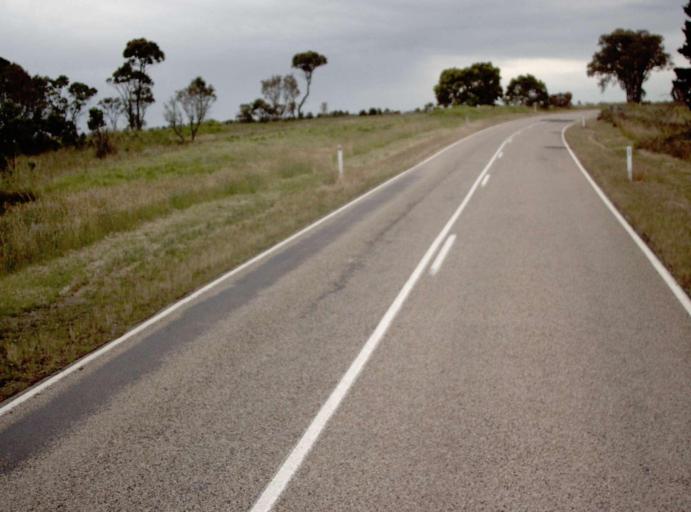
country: AU
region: Victoria
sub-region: East Gippsland
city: Bairnsdale
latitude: -37.9515
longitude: 147.5178
